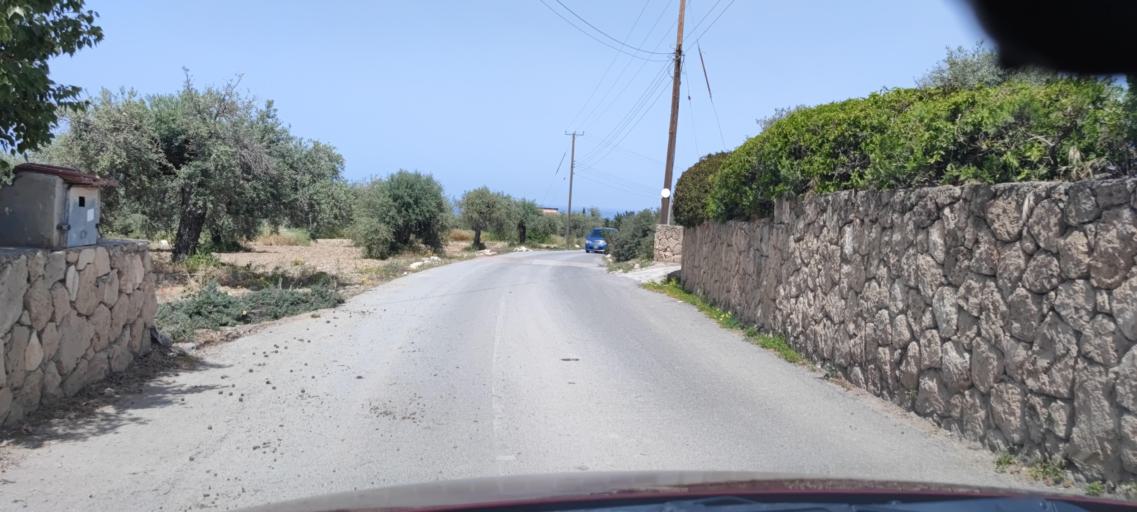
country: CY
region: Keryneia
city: Kyrenia
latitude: 35.3184
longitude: 33.3646
